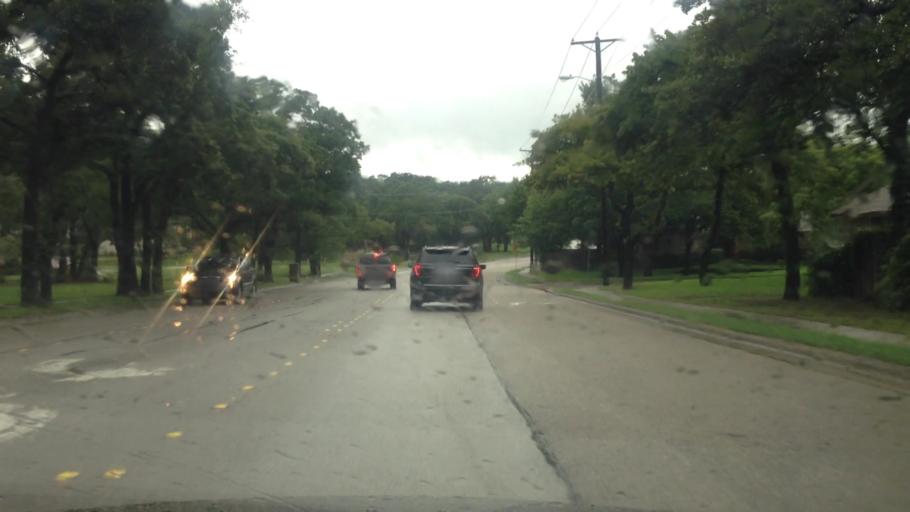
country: US
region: Texas
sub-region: Tarrant County
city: Watauga
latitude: 32.8919
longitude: -97.2184
